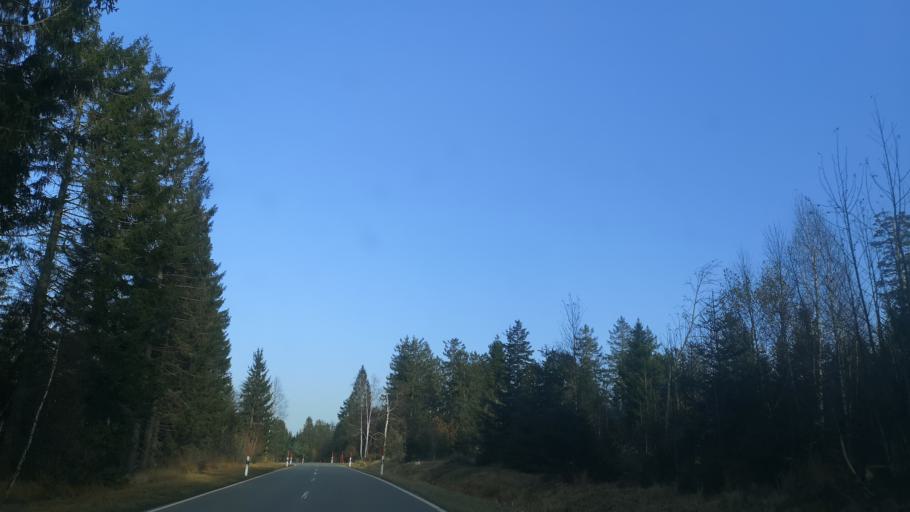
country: DE
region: Baden-Wuerttemberg
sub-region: Freiburg Region
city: Bad Peterstal-Griesbach
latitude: 48.4937
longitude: 8.2499
